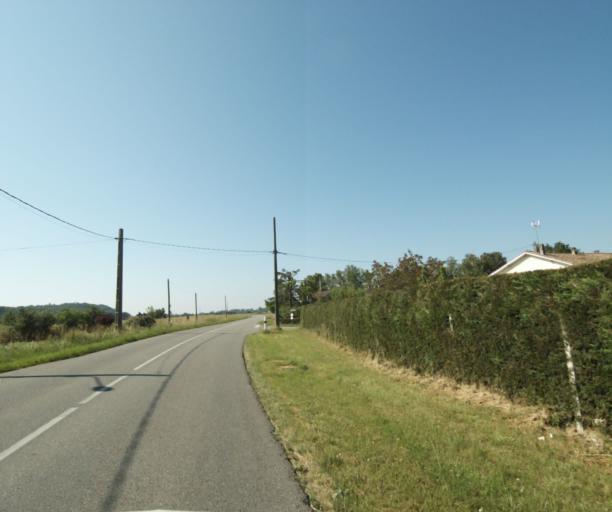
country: FR
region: Midi-Pyrenees
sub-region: Departement du Tarn-et-Garonne
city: Bressols
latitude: 43.9667
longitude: 1.3582
